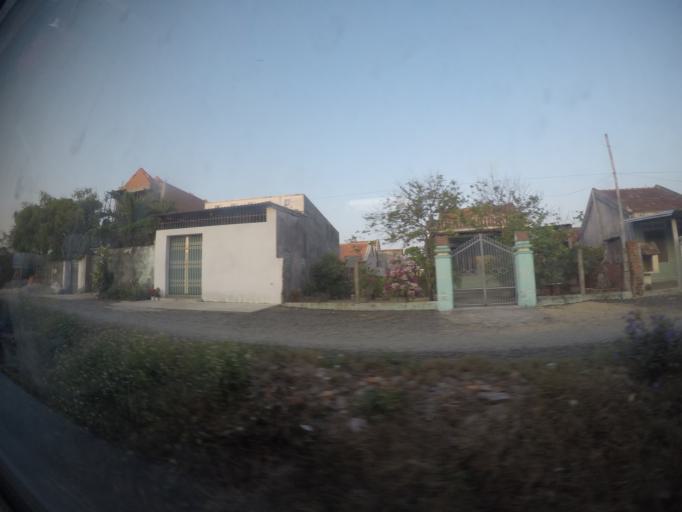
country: VN
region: Phu Yen
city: Tuy Hoa
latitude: 13.1075
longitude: 109.2882
